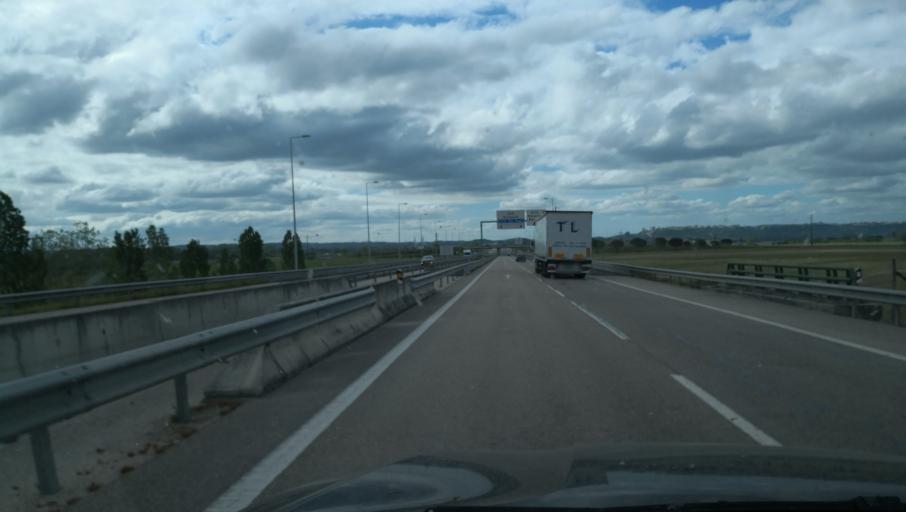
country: PT
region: Santarem
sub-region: Almeirim
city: Almeirim
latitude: 39.1872
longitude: -8.6426
